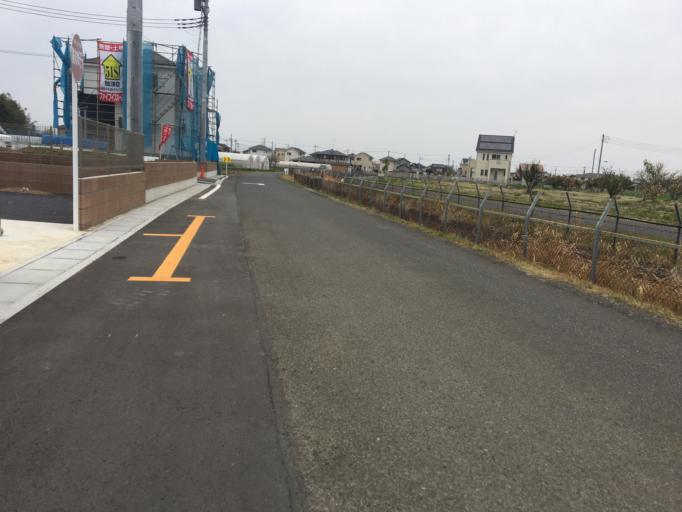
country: JP
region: Saitama
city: Kazo
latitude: 36.1094
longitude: 139.5939
